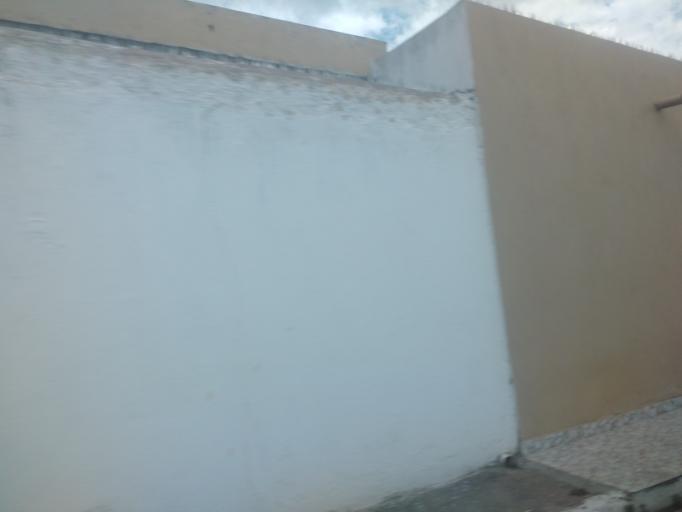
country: BR
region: Alagoas
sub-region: Uniao Dos Palmares
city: Uniao dos Palmares
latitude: -9.1642
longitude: -36.0284
